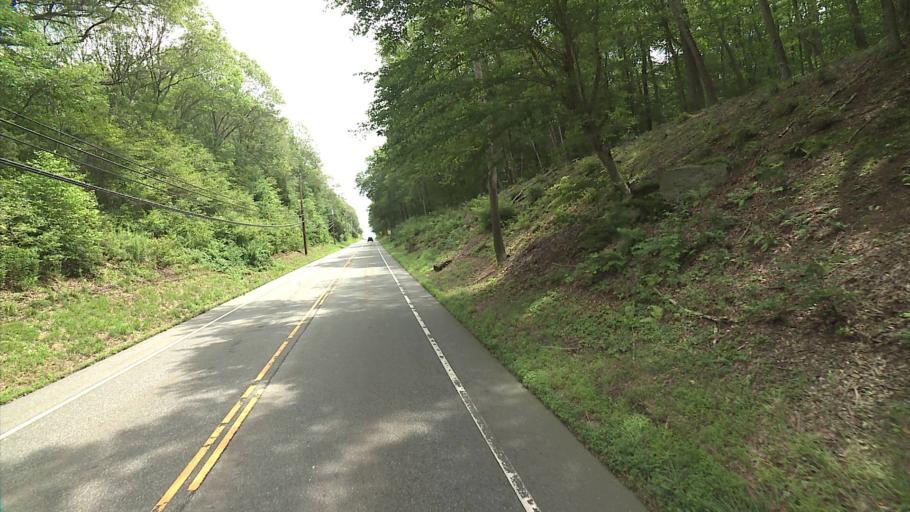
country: US
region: Connecticut
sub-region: New Haven County
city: Madison
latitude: 41.3591
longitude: -72.5754
